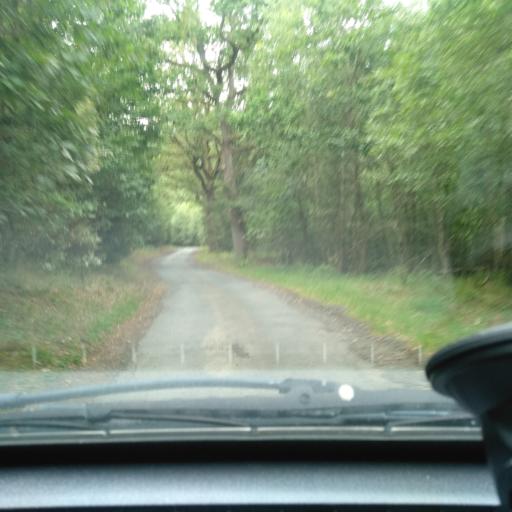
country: DE
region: Hesse
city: Dillenburg
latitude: 50.8071
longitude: 8.3255
